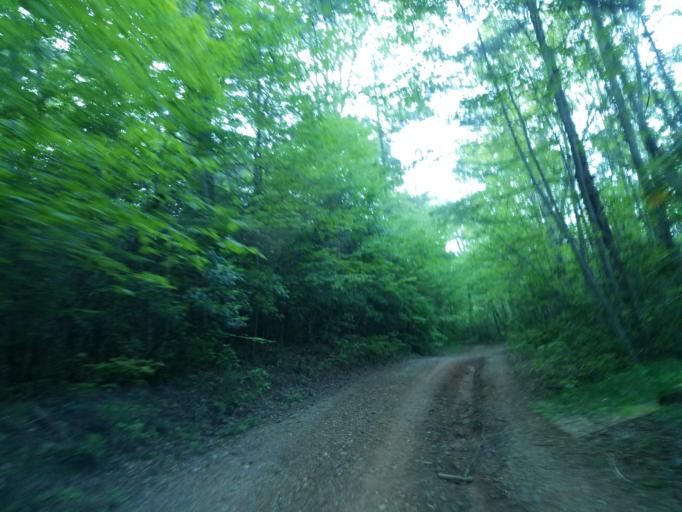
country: US
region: Georgia
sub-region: Lumpkin County
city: Dahlonega
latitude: 34.6675
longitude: -84.1318
